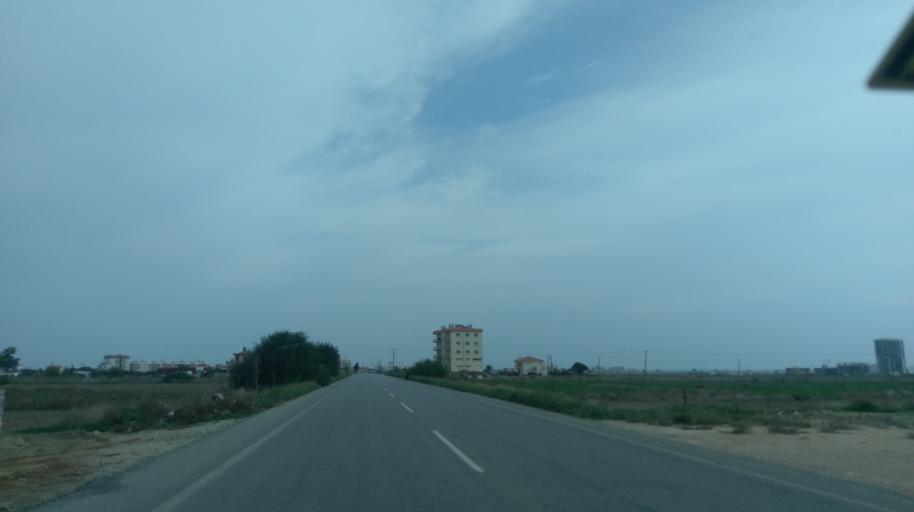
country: CY
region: Ammochostos
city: Trikomo
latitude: 35.2792
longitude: 33.8881
